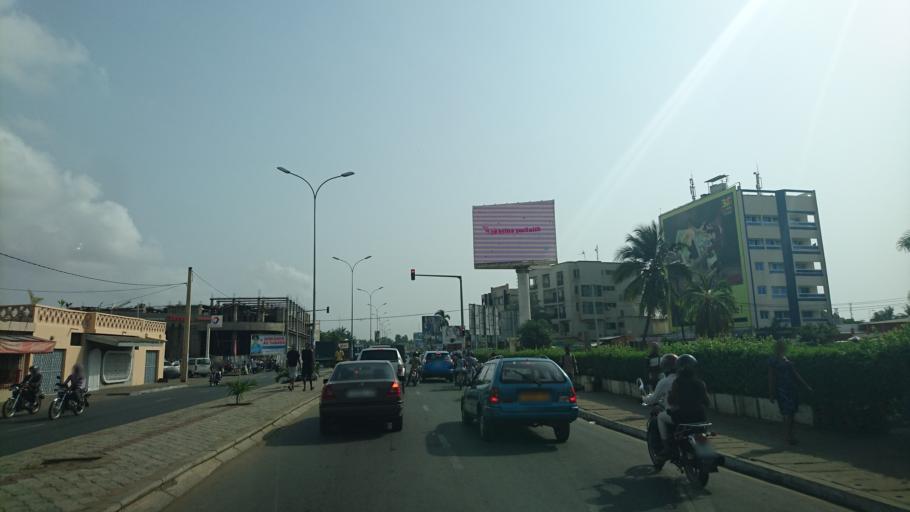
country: TG
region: Maritime
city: Lome
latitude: 6.1356
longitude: 1.2184
